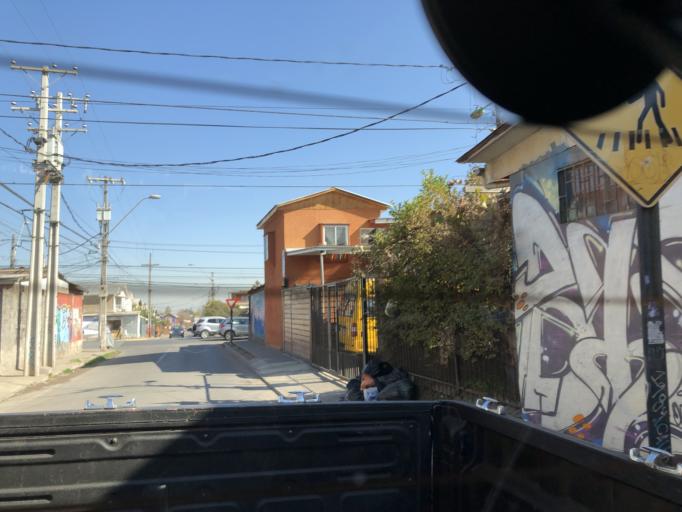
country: CL
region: Santiago Metropolitan
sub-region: Provincia de Cordillera
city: Puente Alto
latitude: -33.5711
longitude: -70.5658
